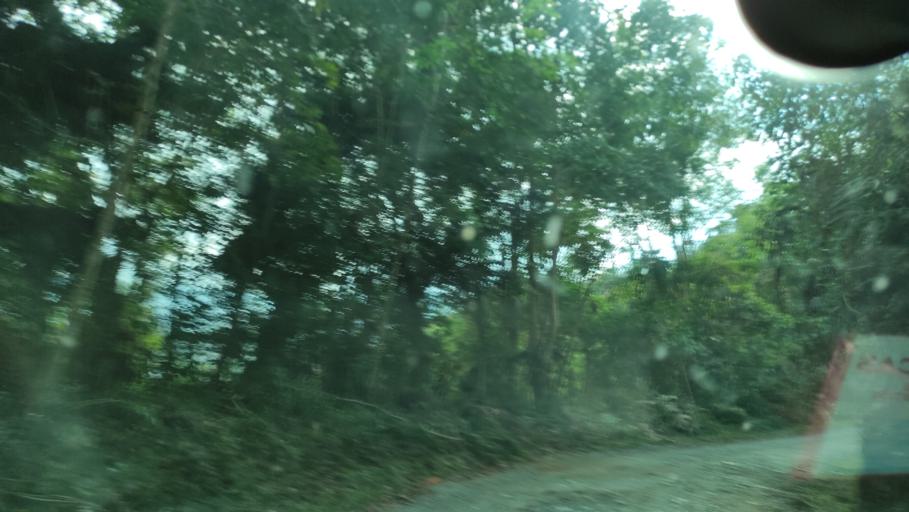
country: CO
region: Valle del Cauca
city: San Pedro
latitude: 3.8801
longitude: -76.1589
